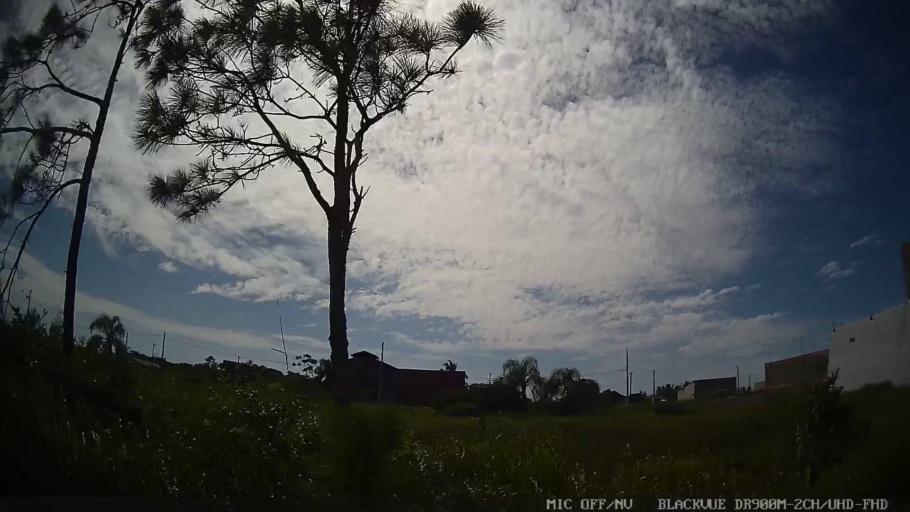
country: BR
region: Sao Paulo
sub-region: Iguape
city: Iguape
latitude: -24.7813
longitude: -47.6083
